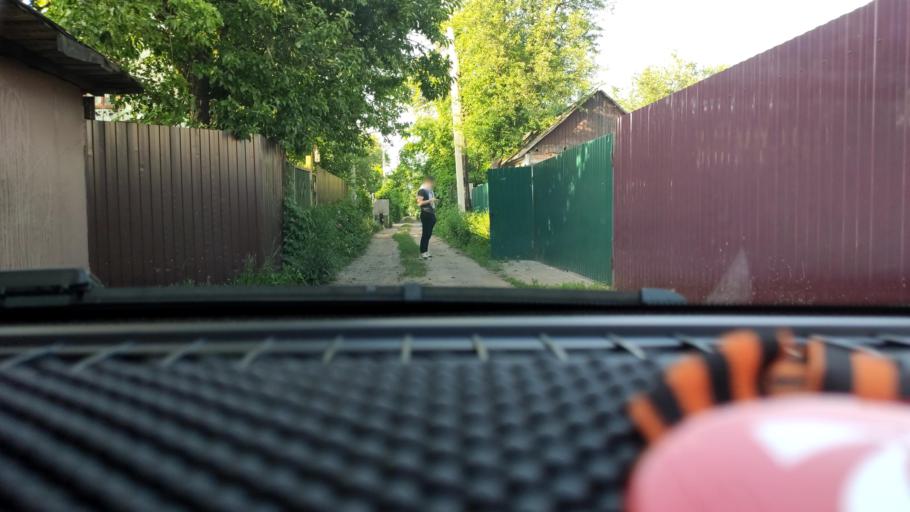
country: RU
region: Voronezj
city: Maslovka
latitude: 51.5920
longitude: 39.1623
